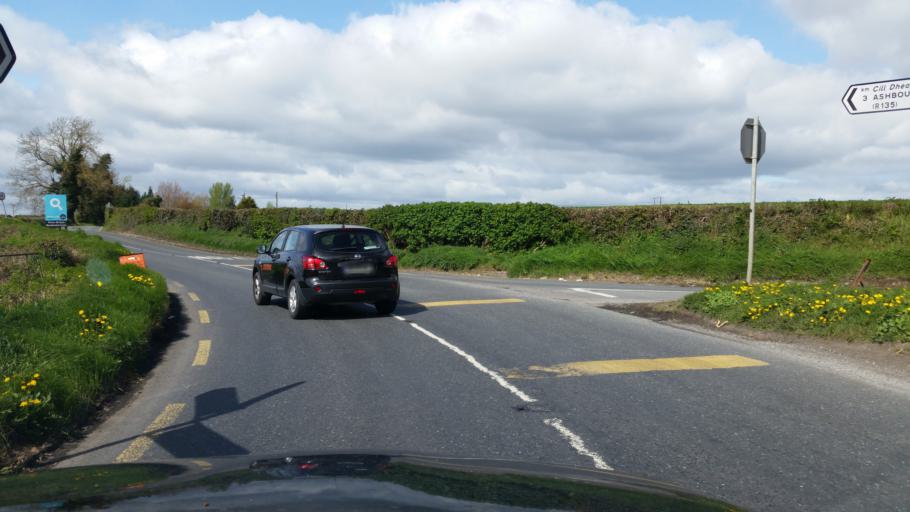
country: IE
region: Leinster
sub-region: An Mhi
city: Ashbourne
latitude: 53.4948
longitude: -6.3725
